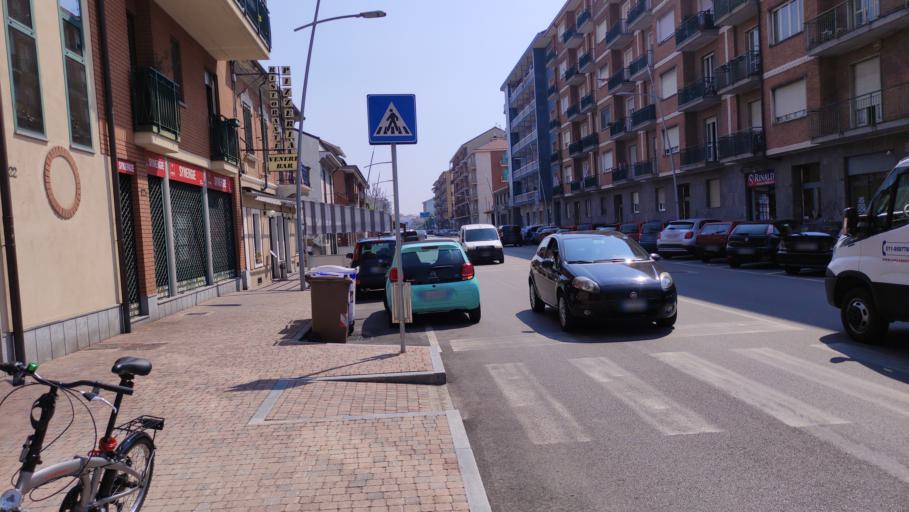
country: IT
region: Piedmont
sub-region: Provincia di Torino
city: Nichelino
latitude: 45.0041
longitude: 7.6626
